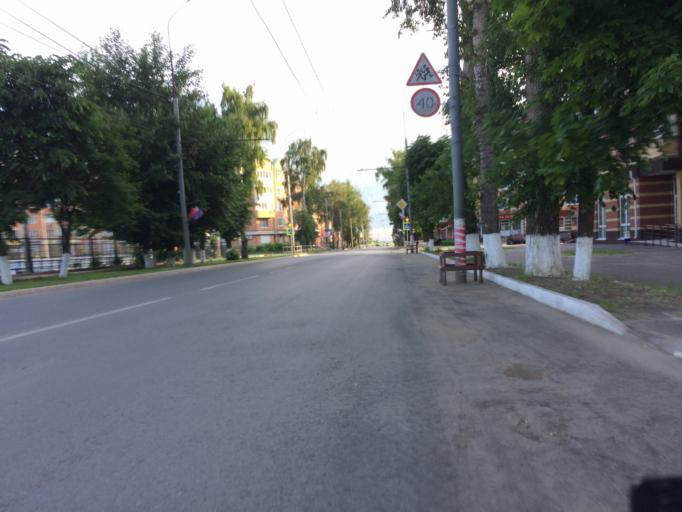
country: RU
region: Mariy-El
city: Medvedevo
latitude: 56.6356
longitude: 47.8033
